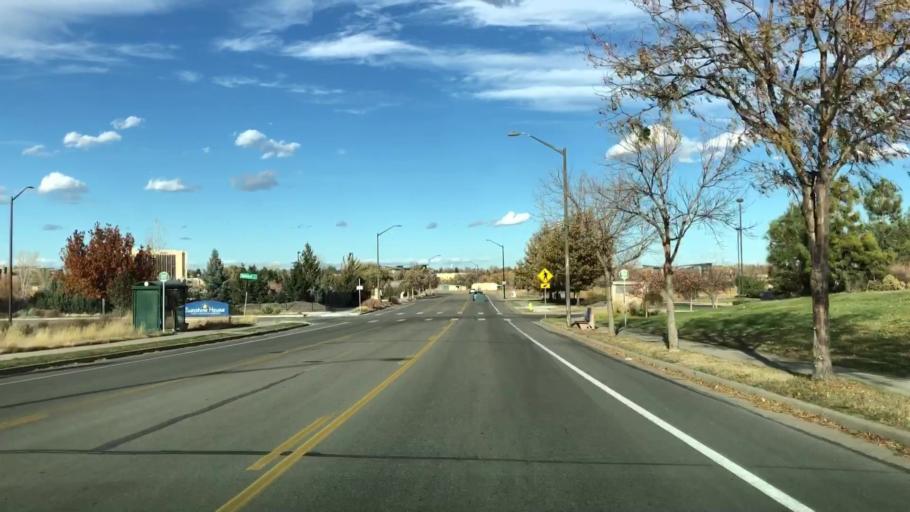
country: US
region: Colorado
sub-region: Larimer County
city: Fort Collins
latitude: 40.5600
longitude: -105.0858
